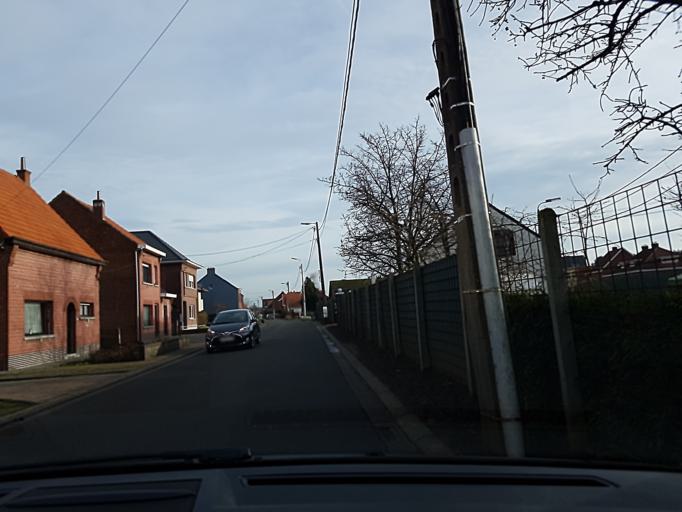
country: BE
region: Flanders
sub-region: Provincie Vlaams-Brabant
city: Haacht
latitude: 50.9743
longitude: 4.6453
